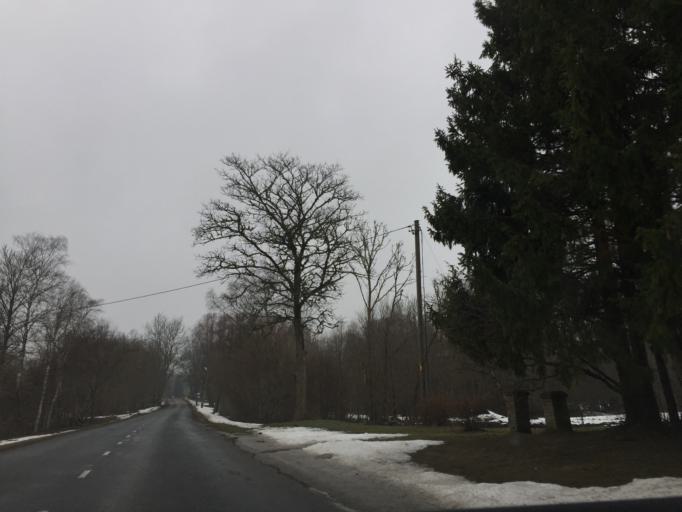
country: EE
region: Saare
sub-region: Orissaare vald
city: Orissaare
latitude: 58.4065
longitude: 22.7918
